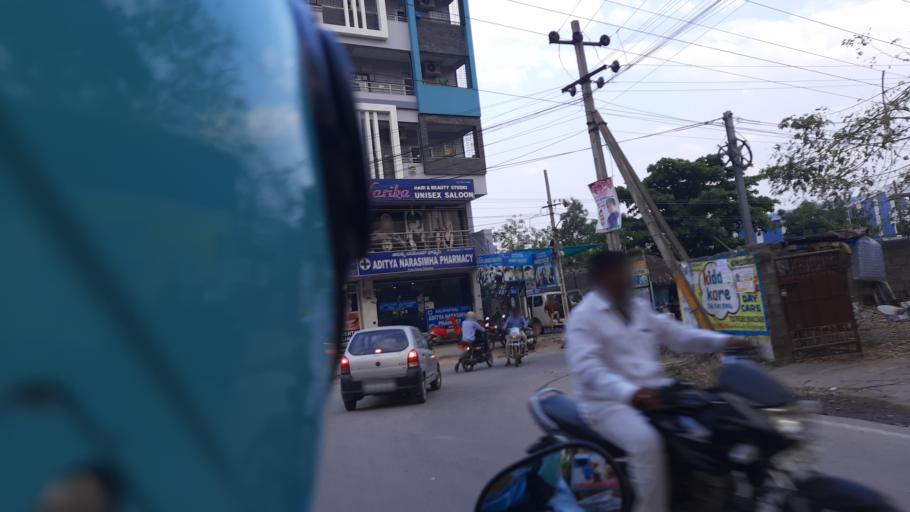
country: IN
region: Telangana
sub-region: Rangareddi
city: Kukatpalli
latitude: 17.4961
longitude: 78.4201
